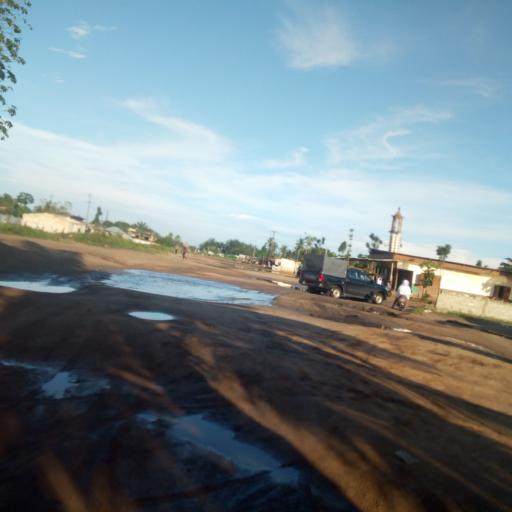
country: BJ
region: Atlantique
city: Hevie
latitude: 6.3871
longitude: 2.2722
